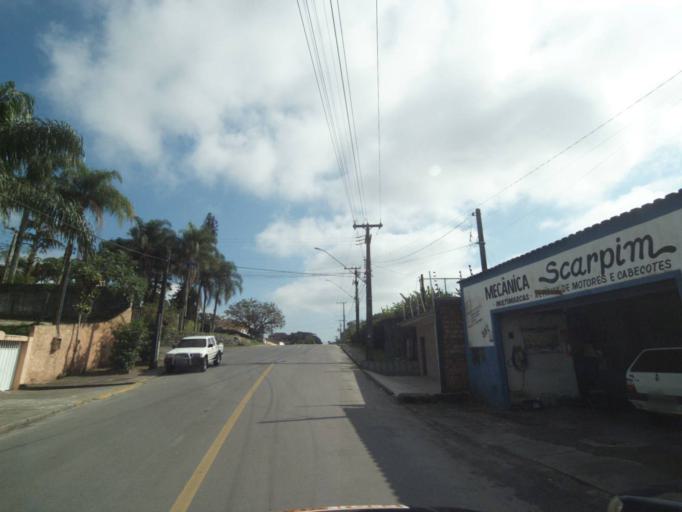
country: BR
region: Parana
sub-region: Paranagua
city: Paranagua
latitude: -25.5261
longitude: -48.5116
